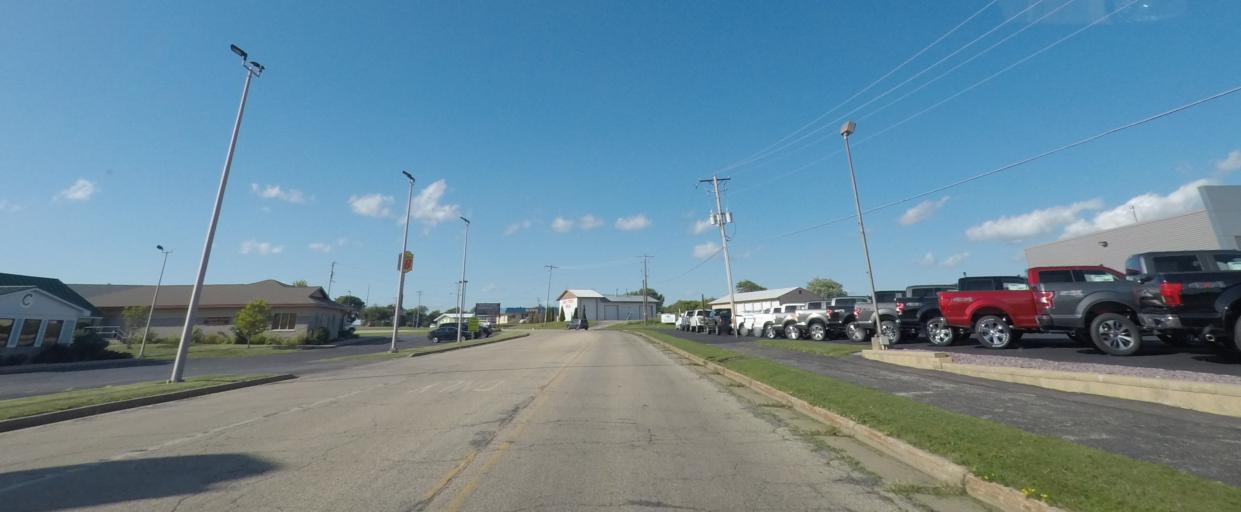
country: US
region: Wisconsin
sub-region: Iowa County
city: Dodgeville
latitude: 42.9748
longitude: -90.1263
